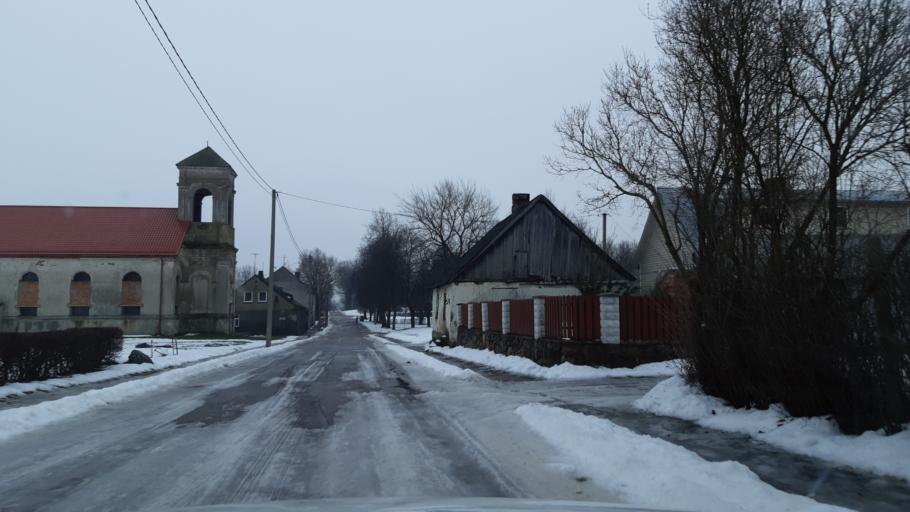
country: LT
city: Virbalis
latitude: 54.6275
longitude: 22.8195
